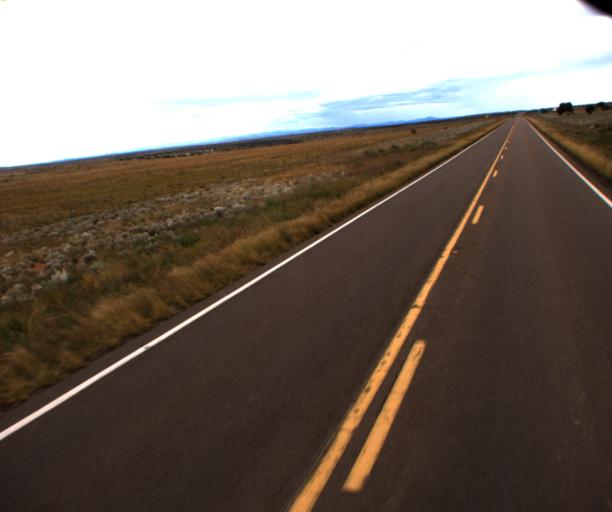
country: US
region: Arizona
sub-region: Navajo County
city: Snowflake
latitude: 34.6041
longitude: -110.0890
